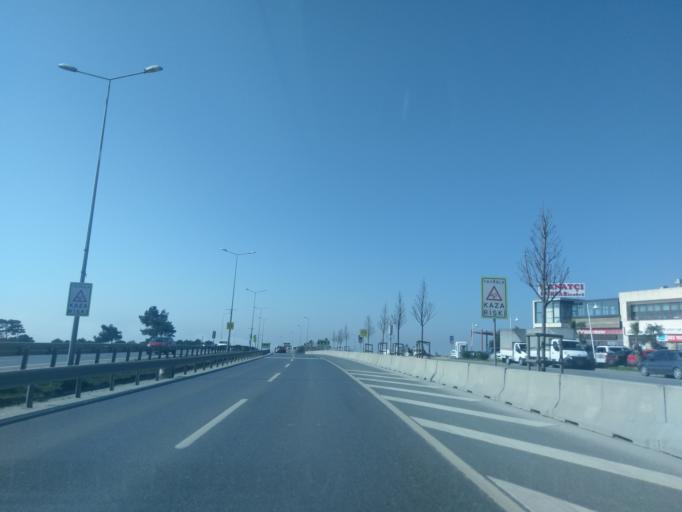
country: TR
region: Istanbul
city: Gurpinar
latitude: 41.0256
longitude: 28.6196
